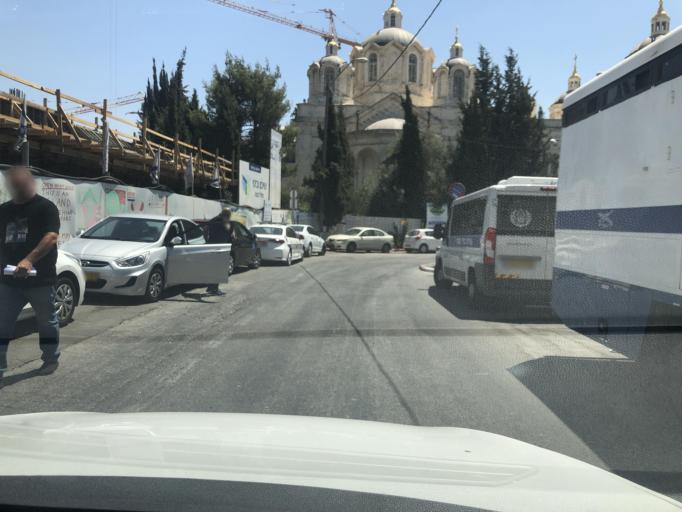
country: IL
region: Jerusalem
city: West Jerusalem
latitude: 31.7821
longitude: 35.2227
